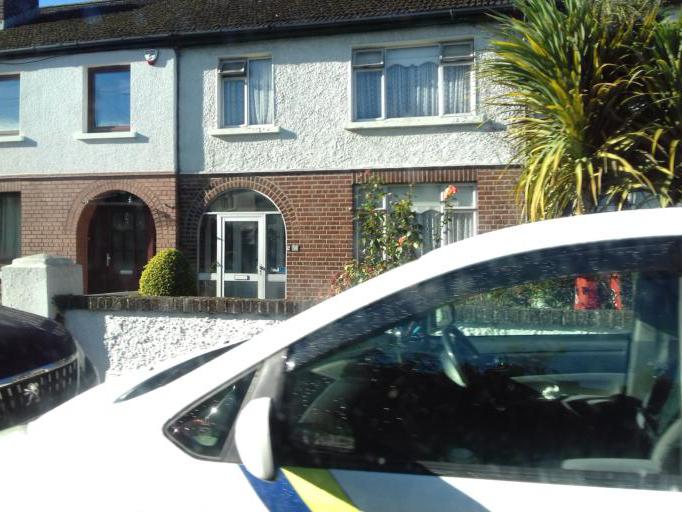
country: IE
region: Leinster
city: Cabra
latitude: 53.3630
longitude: -6.3097
